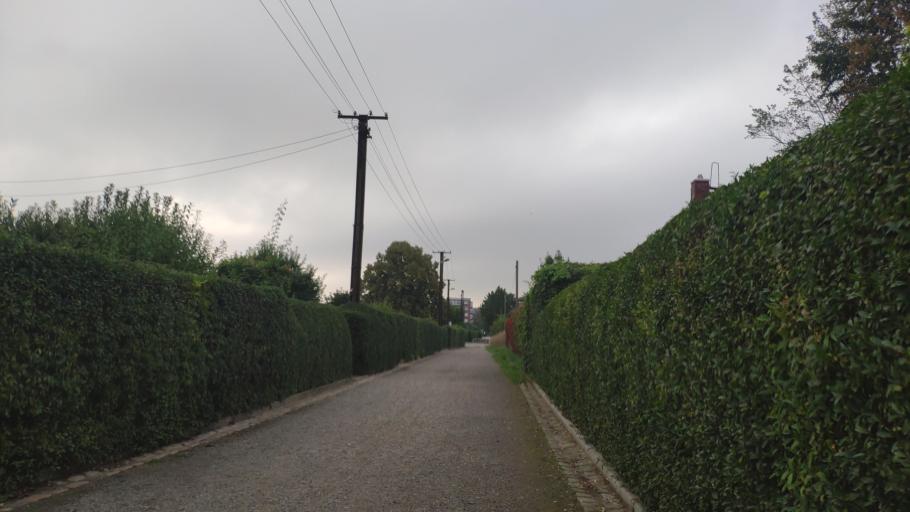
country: DE
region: Saxony
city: Hilbersdorf
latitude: 50.8343
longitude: 12.9632
